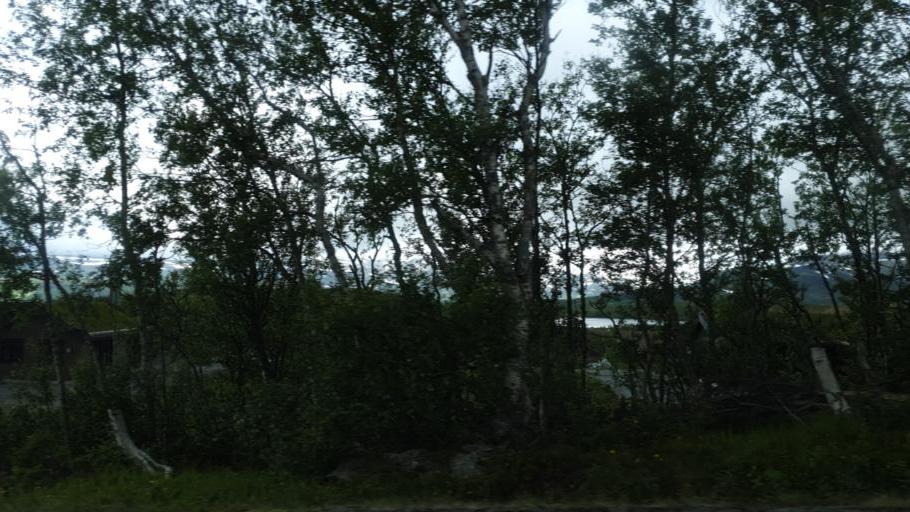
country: NO
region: Oppland
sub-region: Vestre Slidre
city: Slidre
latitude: 61.2578
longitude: 8.8749
